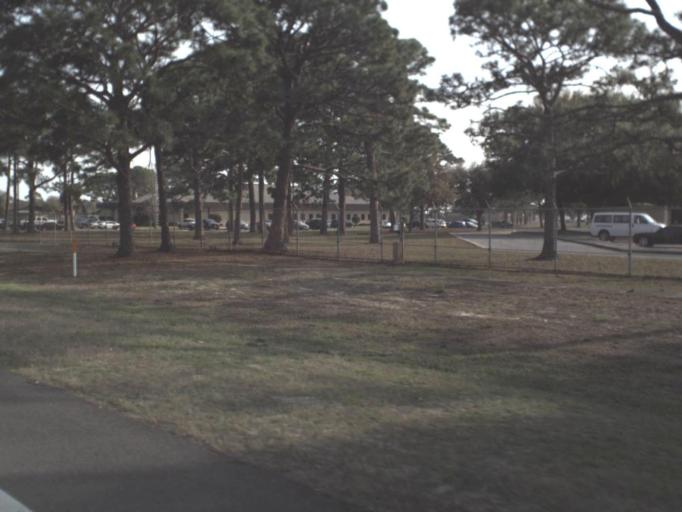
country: US
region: Florida
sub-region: Bay County
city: Tyndall Air Force Base
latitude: 30.0754
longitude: -85.5974
